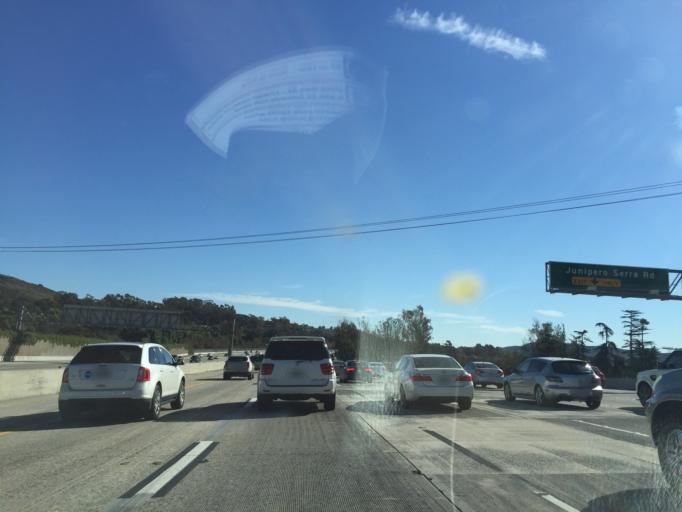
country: US
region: California
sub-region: Orange County
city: San Juan Capistrano
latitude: 33.5295
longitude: -117.6728
